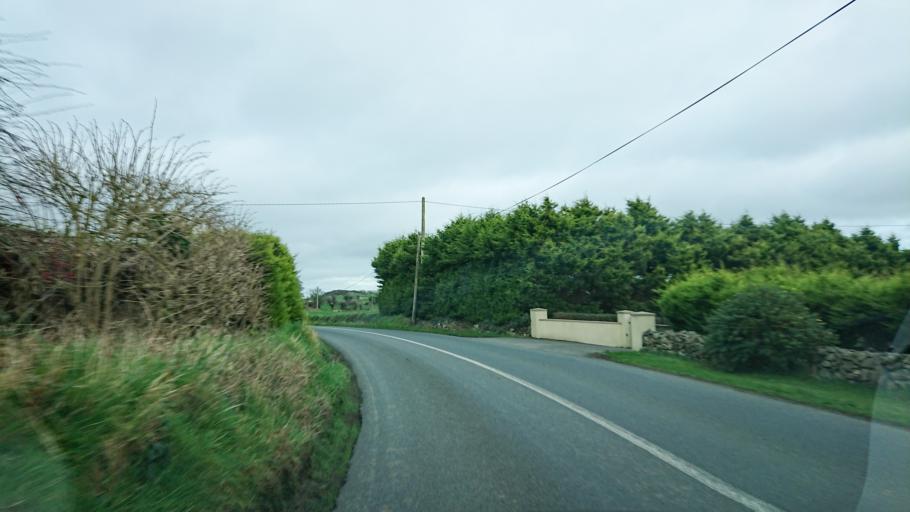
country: IE
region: Leinster
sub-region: Kilkenny
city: Mooncoin
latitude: 52.1931
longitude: -7.2754
